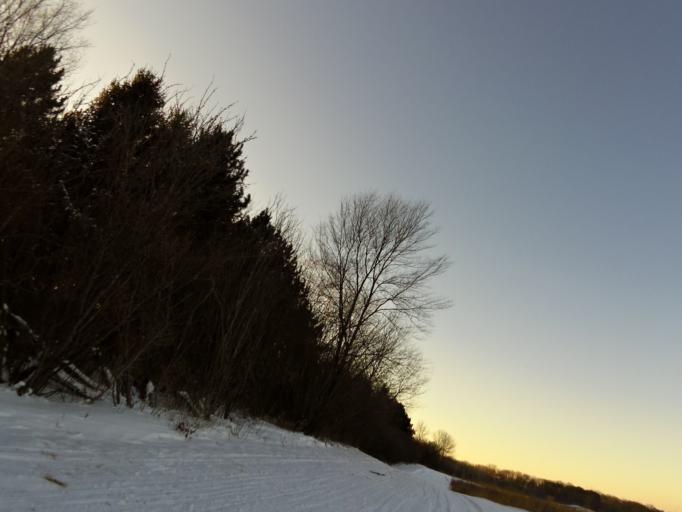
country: US
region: Minnesota
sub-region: Washington County
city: Lake Elmo
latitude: 44.9716
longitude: -92.9171
